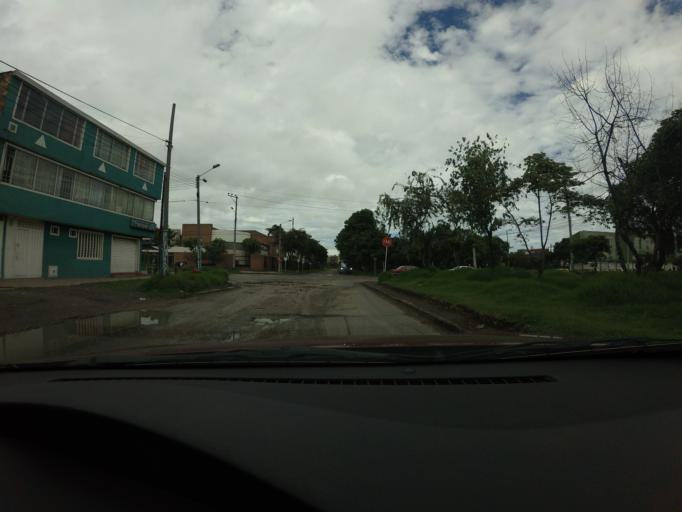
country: CO
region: Bogota D.C.
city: Bogota
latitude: 4.6011
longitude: -74.1485
